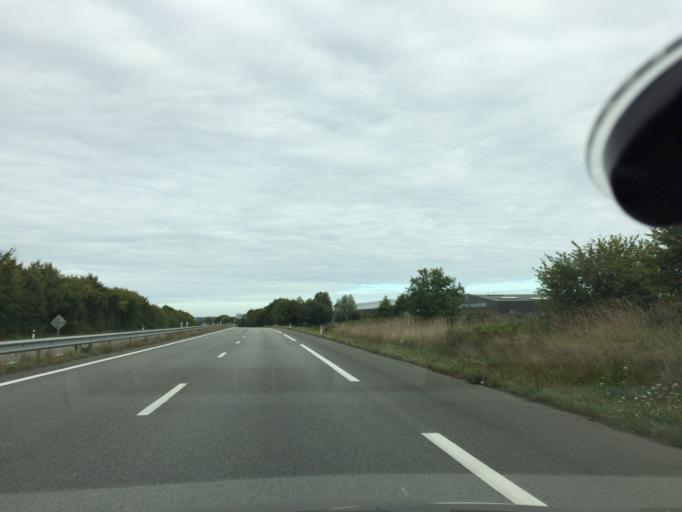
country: FR
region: Brittany
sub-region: Departement d'Ille-et-Vilaine
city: Saint-Domineuc
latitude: 48.3596
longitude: -1.8707
